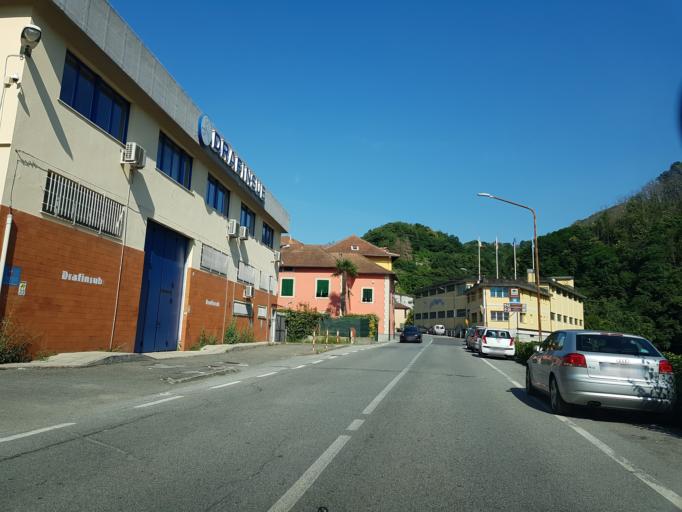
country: IT
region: Liguria
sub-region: Provincia di Genova
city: Manesseno
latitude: 44.4767
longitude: 8.9274
